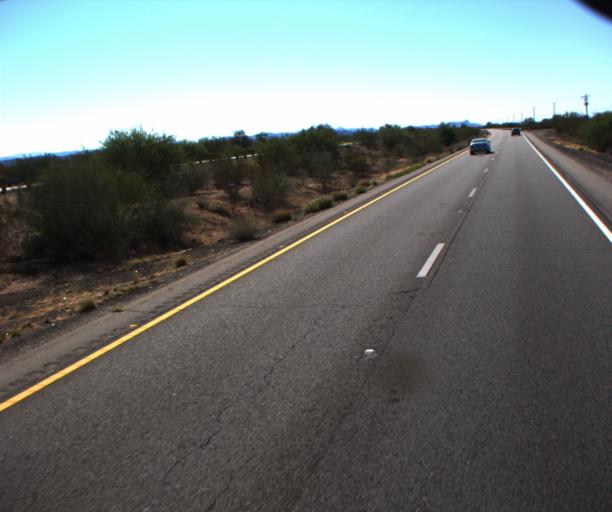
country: US
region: Arizona
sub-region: Pinal County
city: Gold Camp
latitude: 33.3225
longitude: -111.4259
